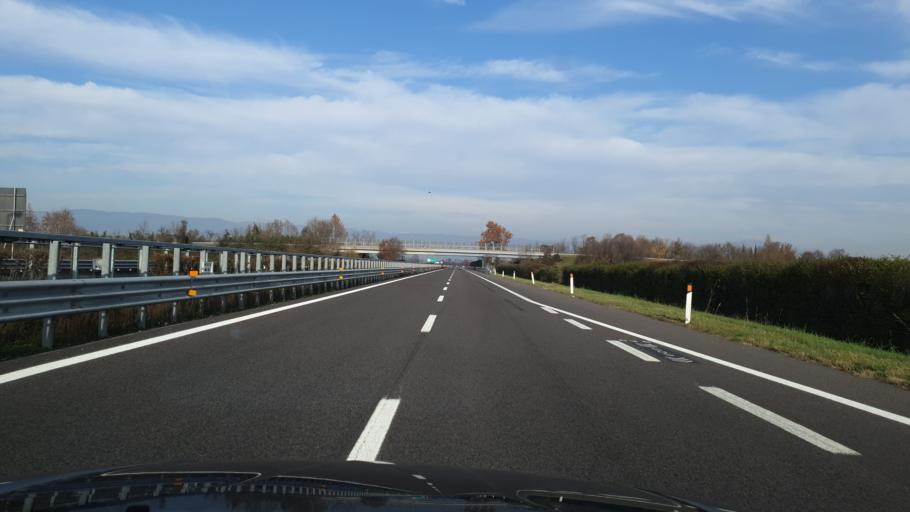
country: IT
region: Veneto
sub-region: Provincia di Vicenza
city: Vigardolo
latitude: 45.5978
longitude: 11.5997
